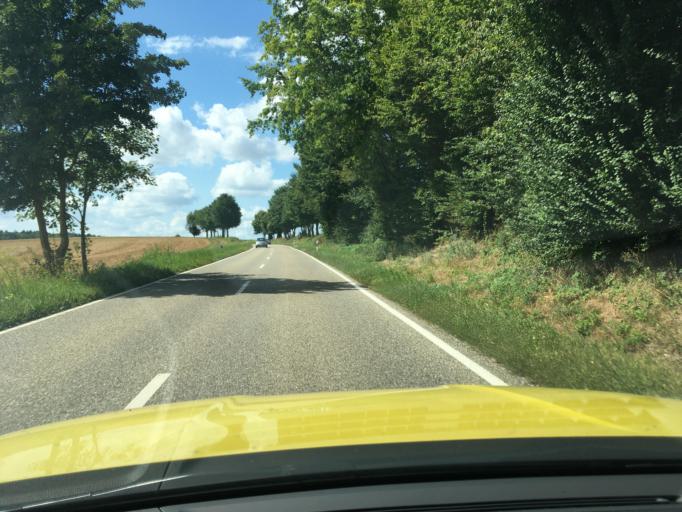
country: DE
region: Baden-Wuerttemberg
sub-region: Regierungsbezirk Stuttgart
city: Massenbachhausen
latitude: 49.1743
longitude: 9.0351
